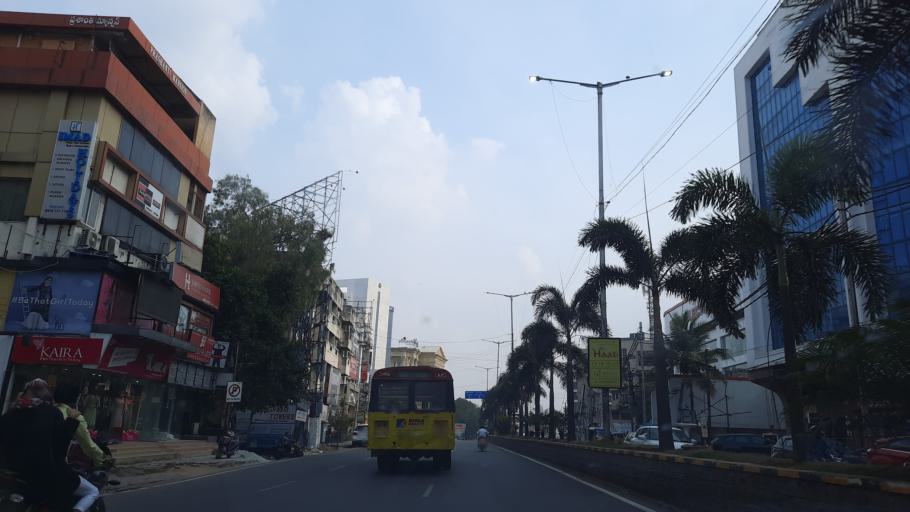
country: IN
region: Telangana
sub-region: Hyderabad
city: Hyderabad
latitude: 17.4095
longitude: 78.4503
